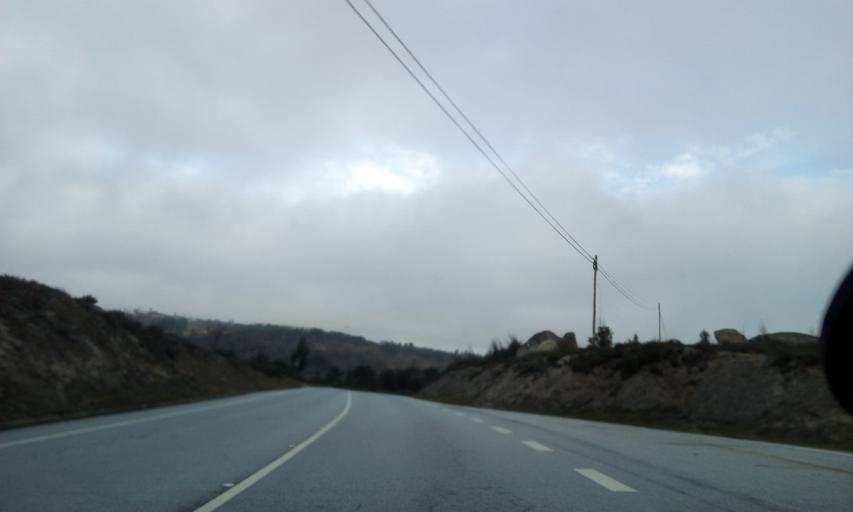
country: PT
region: Guarda
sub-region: Fornos de Algodres
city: Fornos de Algodres
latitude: 40.6678
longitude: -7.4749
